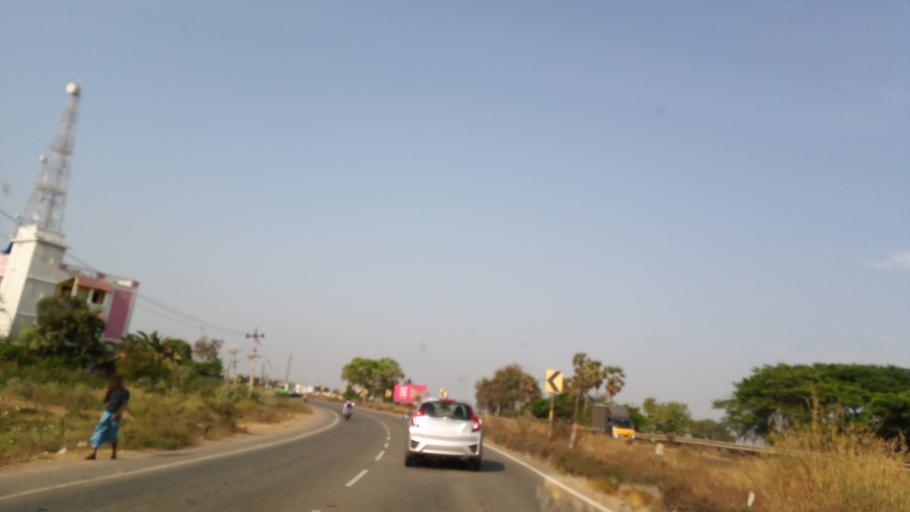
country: IN
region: Tamil Nadu
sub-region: Kancheepuram
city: Sriperumbudur
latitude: 12.9648
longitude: 79.9517
